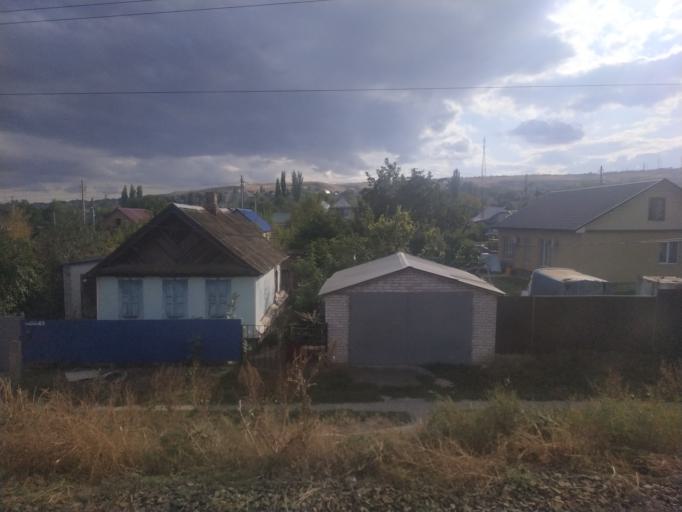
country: RU
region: Volgograd
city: Krasnoslobodsk
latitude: 48.5079
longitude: 44.5419
